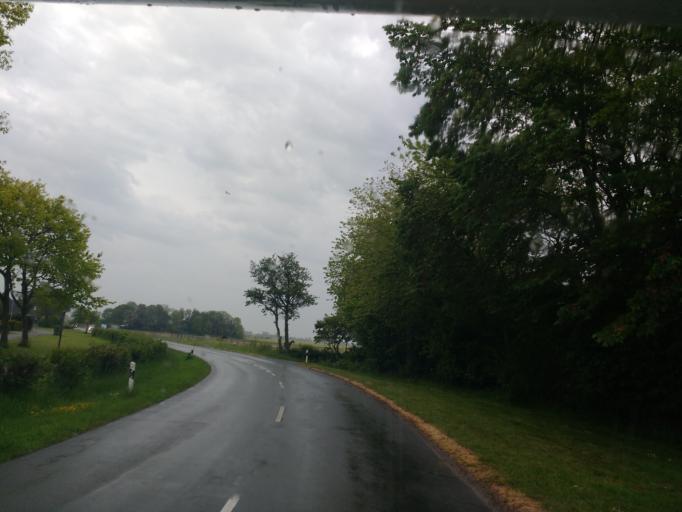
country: DE
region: Lower Saxony
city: Schillig
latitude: 53.6970
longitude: 8.0146
